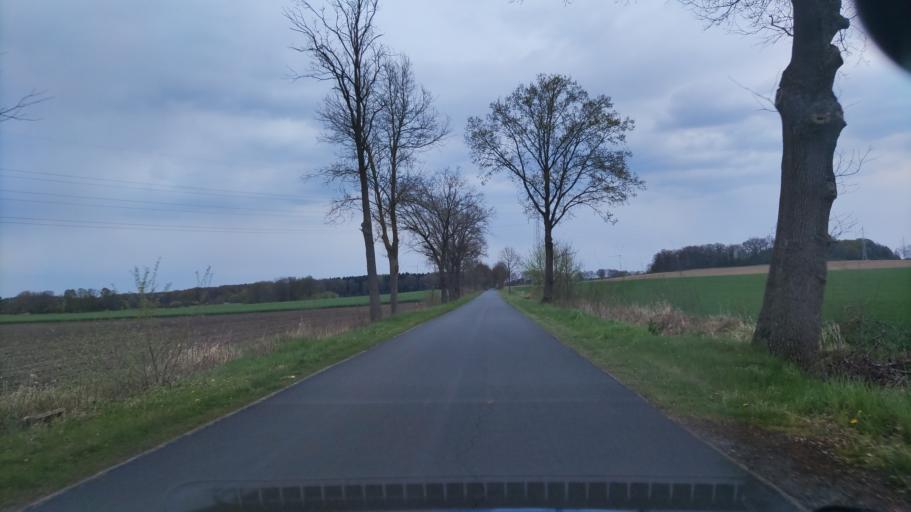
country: DE
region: Lower Saxony
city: Oldendorf
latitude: 53.1592
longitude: 10.2247
